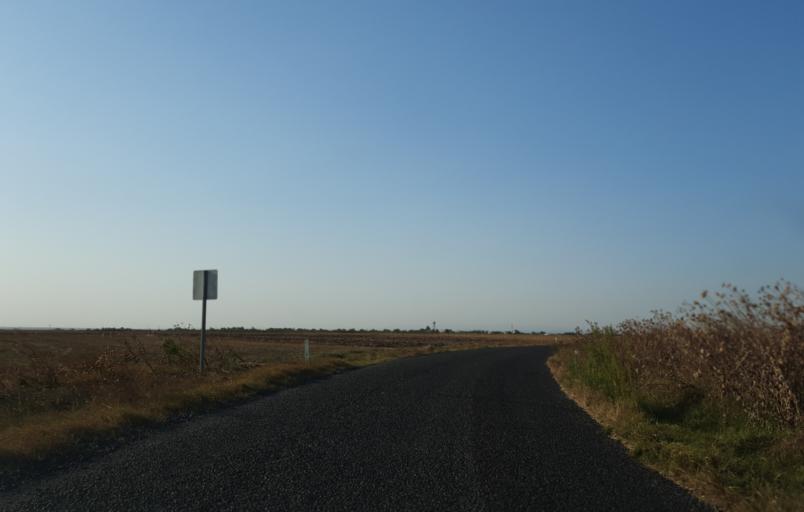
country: TR
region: Tekirdag
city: Beyazkoy
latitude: 41.4209
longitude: 27.7622
